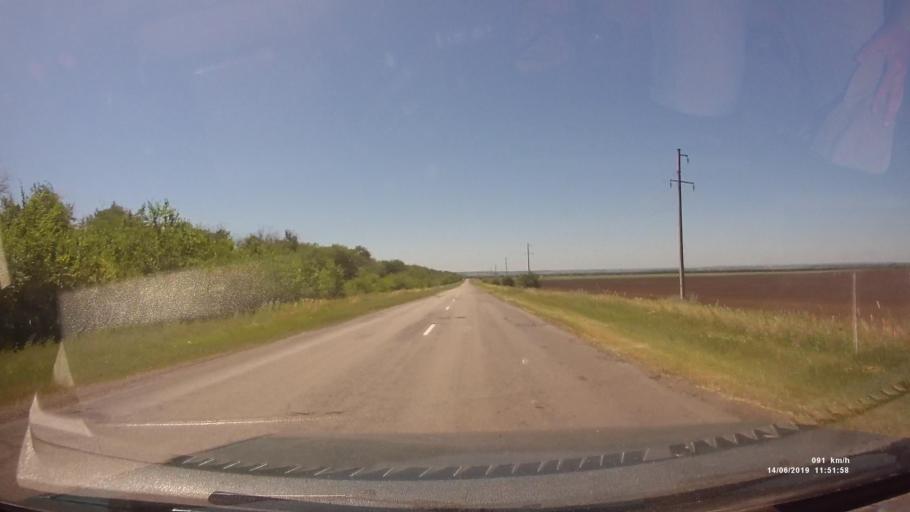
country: RU
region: Rostov
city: Kazanskaya
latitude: 49.8392
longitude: 41.2368
